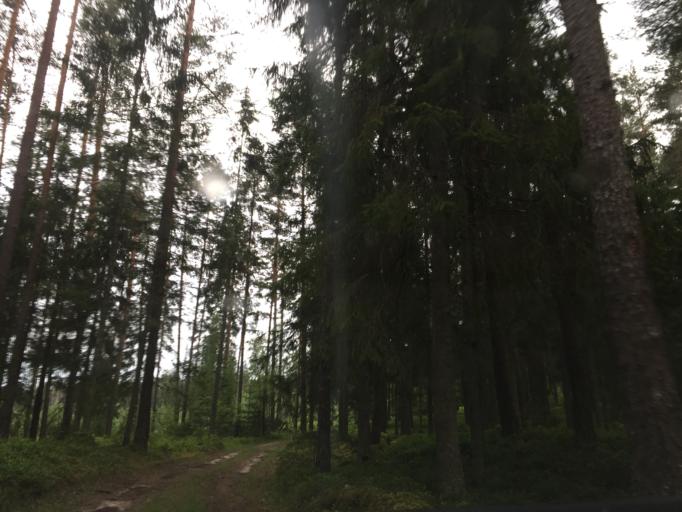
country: LV
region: Tukuma Rajons
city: Tukums
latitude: 57.0195
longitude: 23.0805
